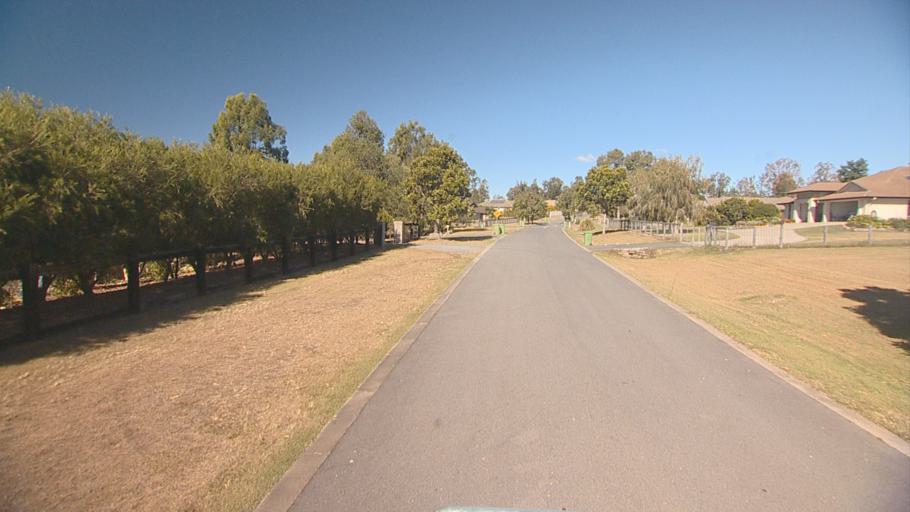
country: AU
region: Queensland
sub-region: Logan
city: North Maclean
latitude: -27.7567
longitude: 152.9643
